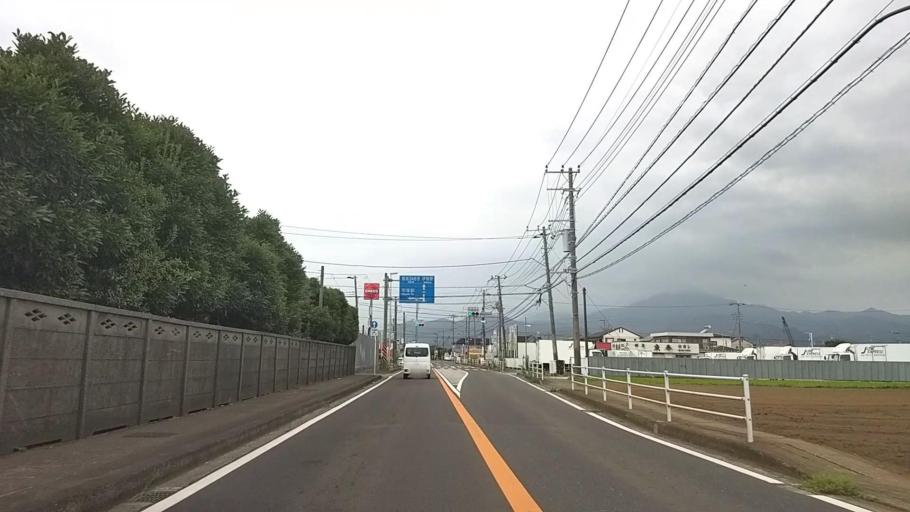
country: JP
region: Kanagawa
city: Isehara
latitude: 35.3780
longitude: 139.3439
